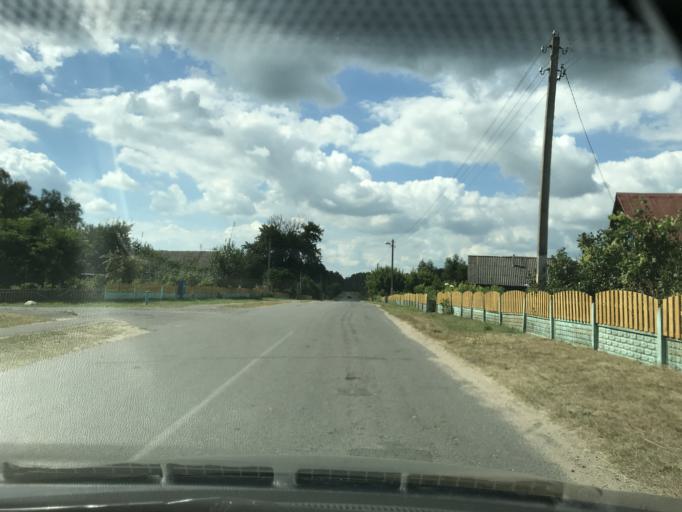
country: BY
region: Mogilev
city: Bykhaw
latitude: 53.5781
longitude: 30.3439
